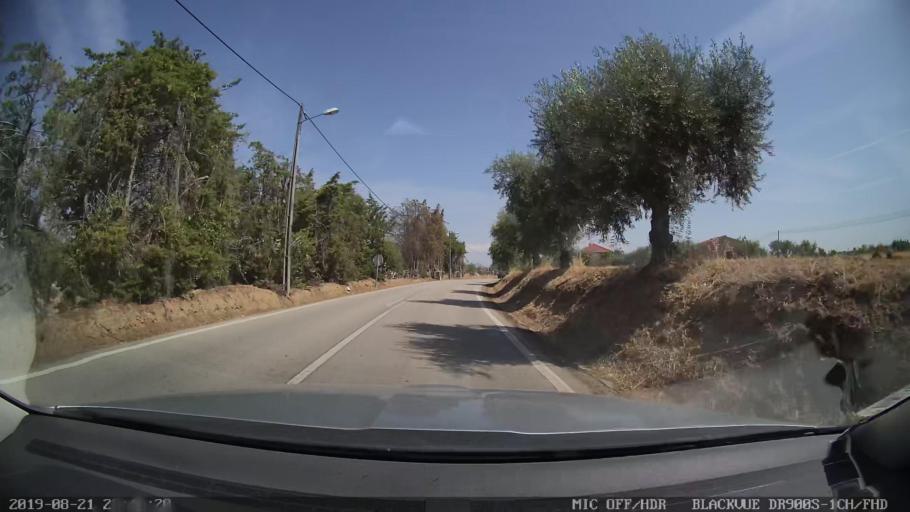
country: PT
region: Castelo Branco
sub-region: Idanha-A-Nova
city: Idanha-a-Nova
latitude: 39.8404
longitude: -7.2590
